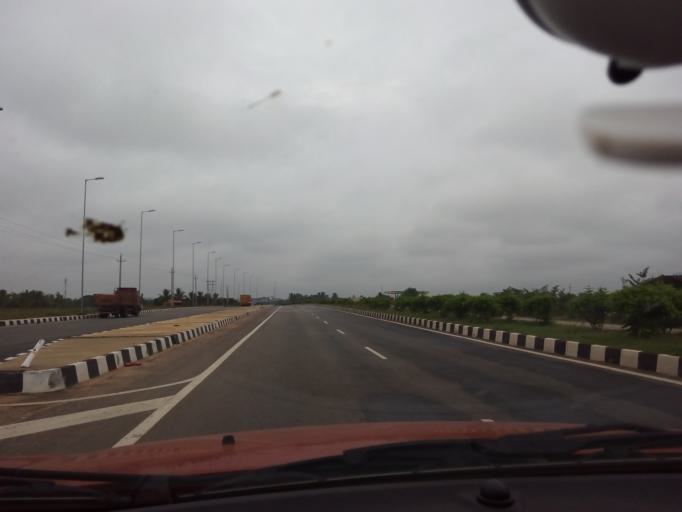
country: IN
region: Karnataka
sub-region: Hassan
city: Shravanabelagola
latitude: 12.9577
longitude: 76.5876
